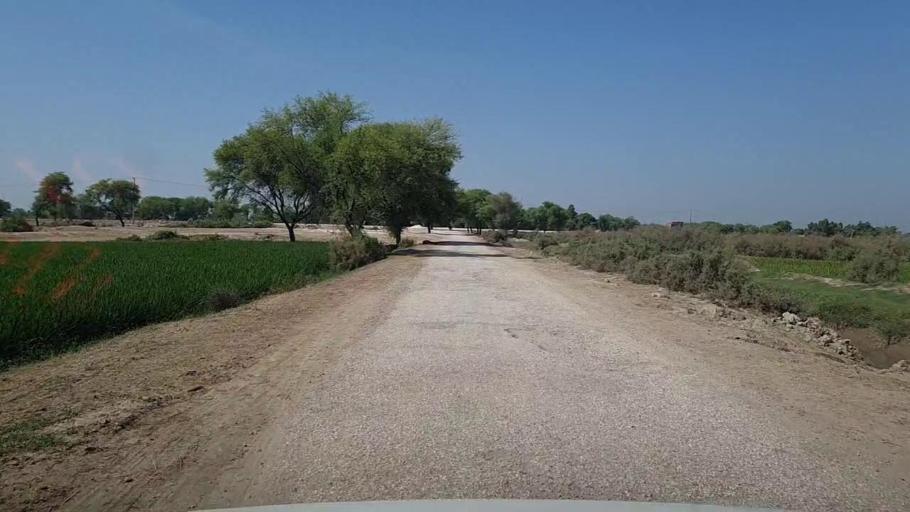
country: PK
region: Sindh
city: Kandhkot
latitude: 28.3387
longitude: 69.3625
